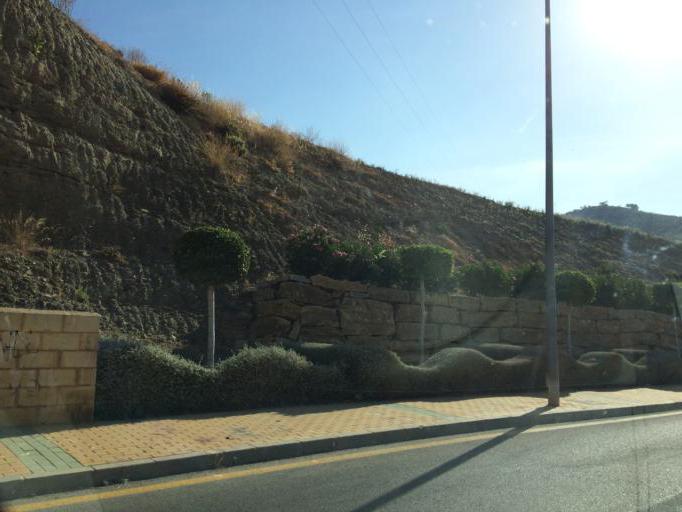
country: ES
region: Andalusia
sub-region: Provincia de Malaga
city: Malaga
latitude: 36.7556
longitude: -4.4190
